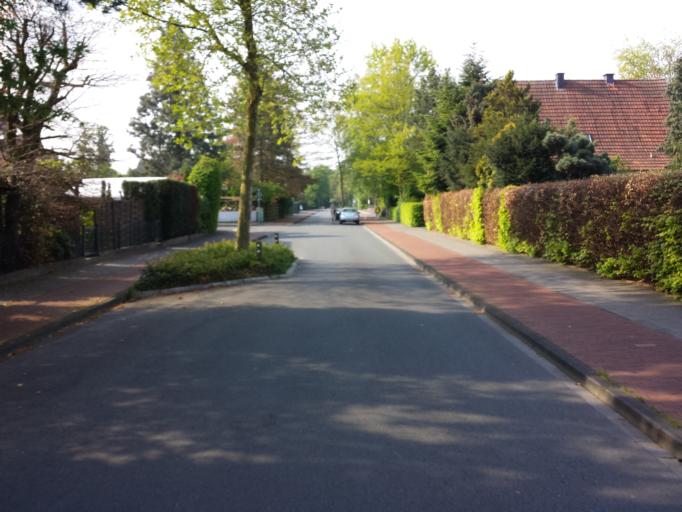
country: DE
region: North Rhine-Westphalia
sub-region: Regierungsbezirk Detmold
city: Guetersloh
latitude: 51.8853
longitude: 8.3685
